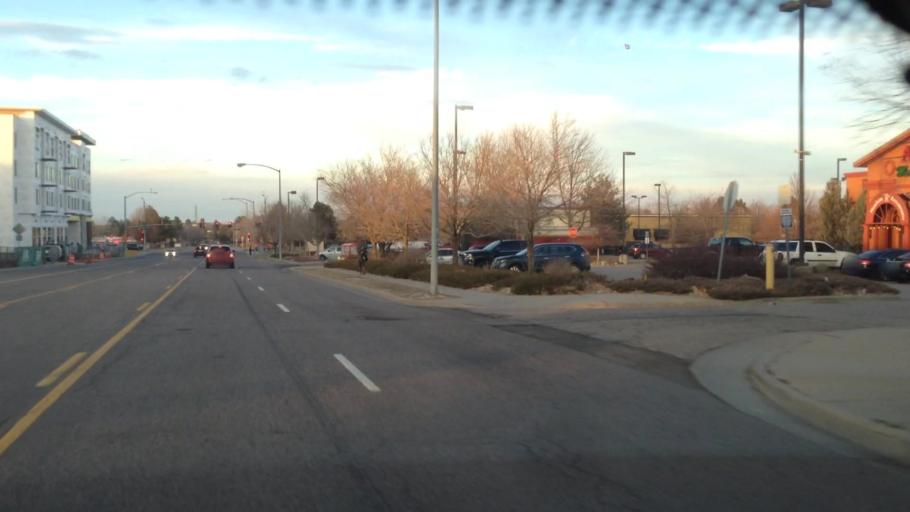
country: US
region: Colorado
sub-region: Adams County
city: Aurora
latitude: 39.6729
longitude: -104.8240
